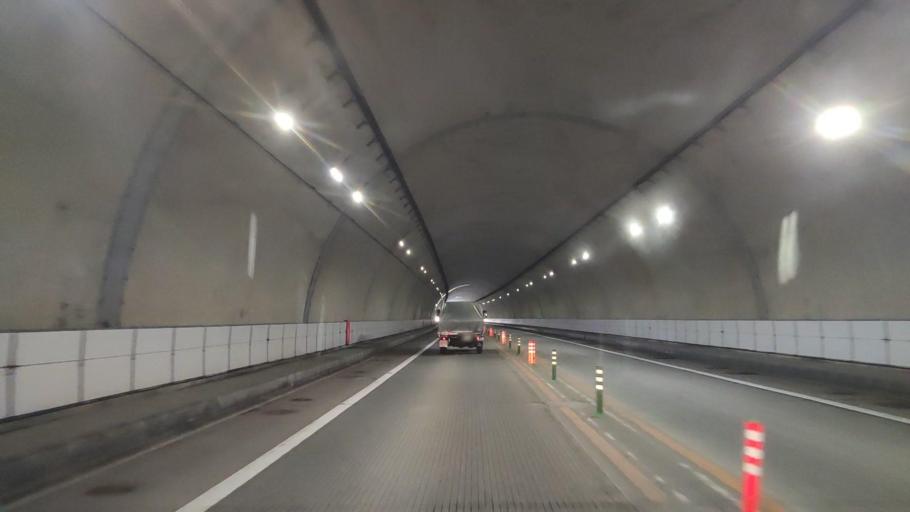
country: JP
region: Gifu
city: Takayama
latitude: 36.1902
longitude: 137.5550
